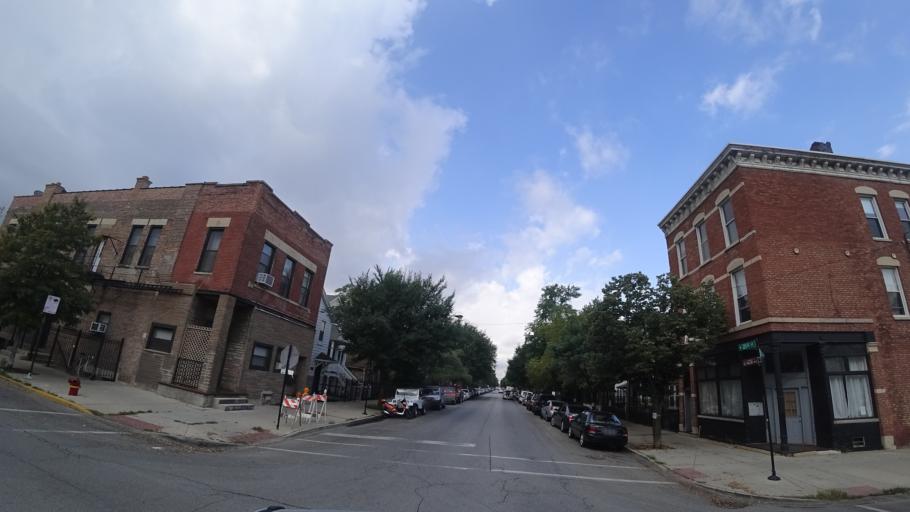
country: US
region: Illinois
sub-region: Cook County
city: Chicago
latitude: 41.8541
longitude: -87.6710
